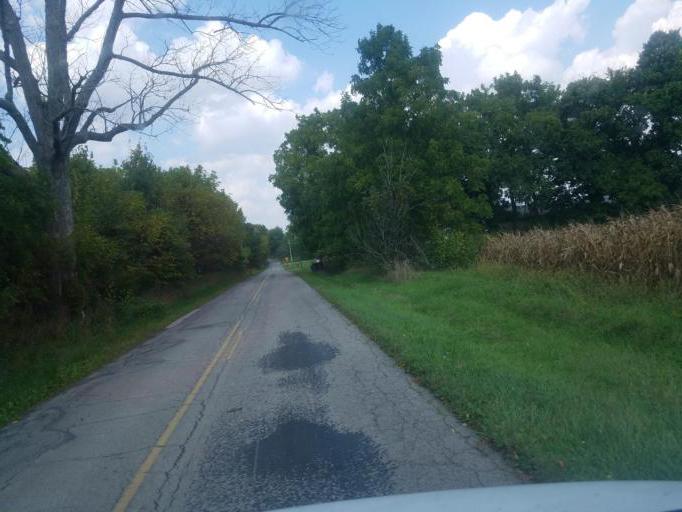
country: US
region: Ohio
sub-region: Hardin County
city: Ada
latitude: 40.6480
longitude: -83.8886
